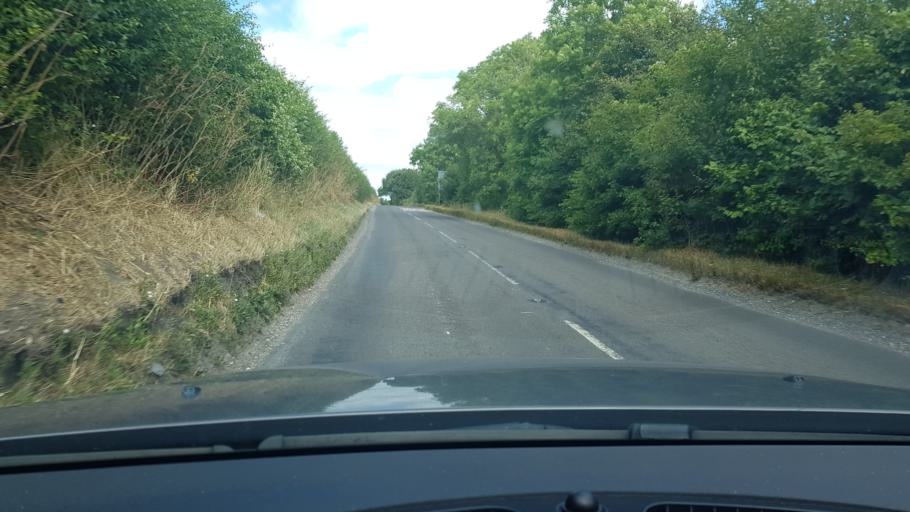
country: GB
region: England
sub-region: Wiltshire
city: Shalbourne
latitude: 51.3639
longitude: -1.5608
